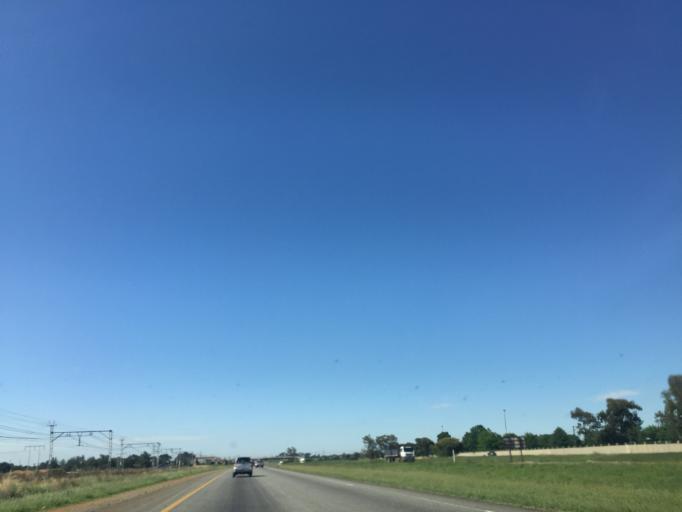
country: ZA
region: Gauteng
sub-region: Sedibeng District Municipality
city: Meyerton
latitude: -26.5819
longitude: 27.9961
